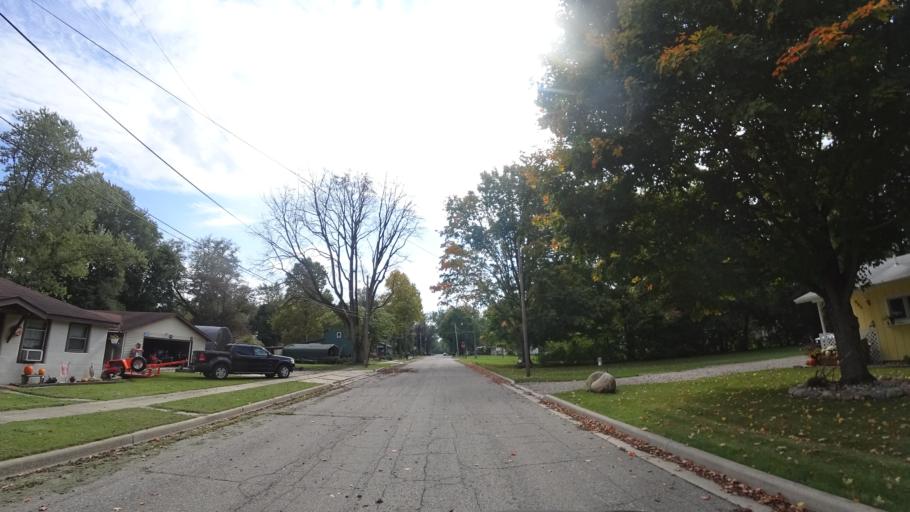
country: US
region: Michigan
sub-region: Saint Joseph County
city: Three Rivers
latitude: 41.9370
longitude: -85.6212
